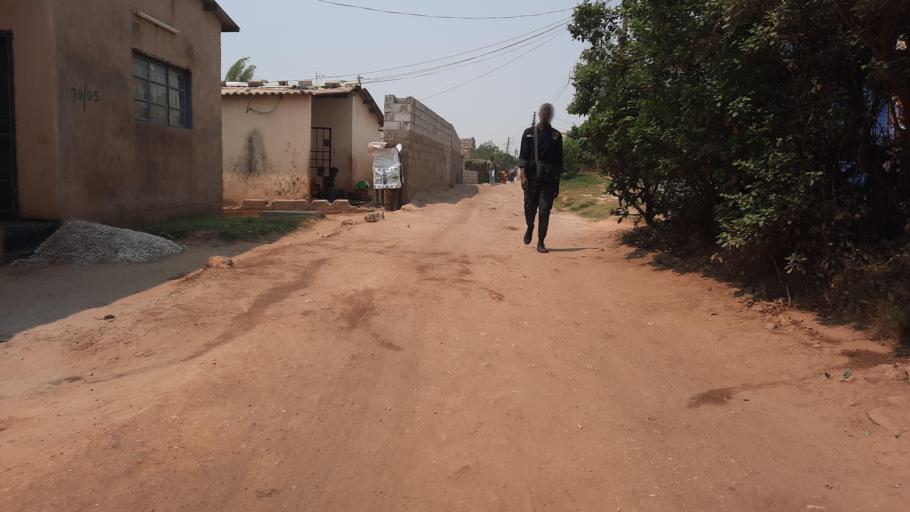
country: ZM
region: Lusaka
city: Lusaka
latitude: -15.3971
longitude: 28.3789
